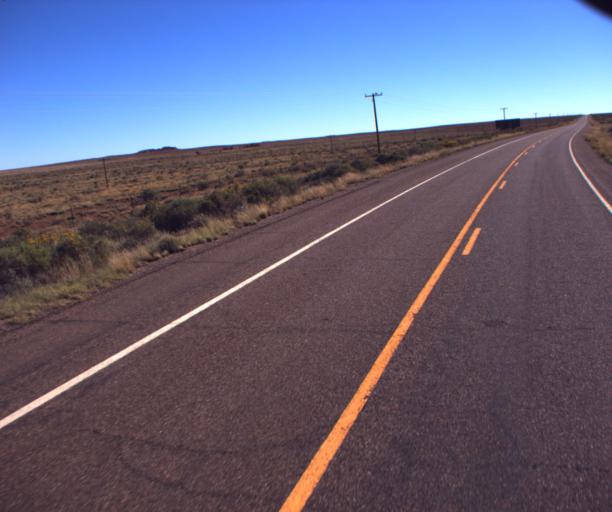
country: US
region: Arizona
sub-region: Navajo County
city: Holbrook
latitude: 34.8840
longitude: -110.0991
